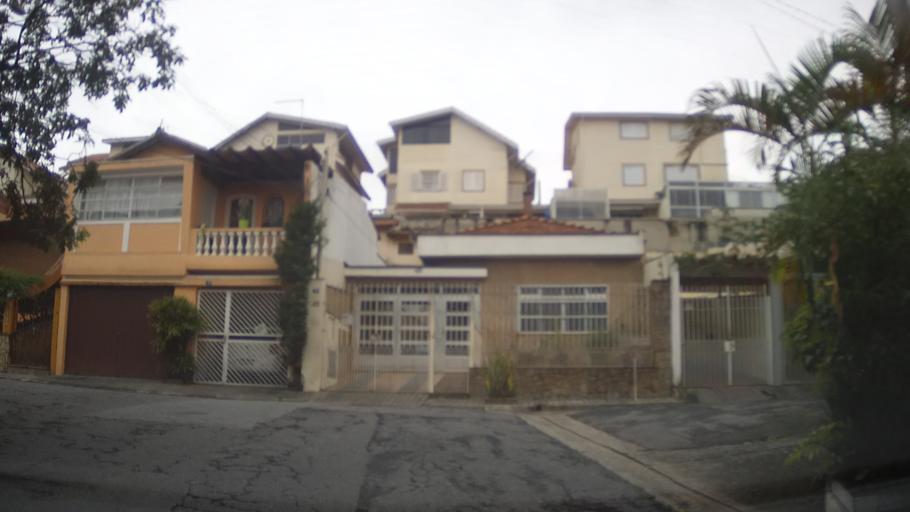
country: BR
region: Sao Paulo
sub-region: Guarulhos
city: Guarulhos
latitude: -23.5015
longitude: -46.5521
